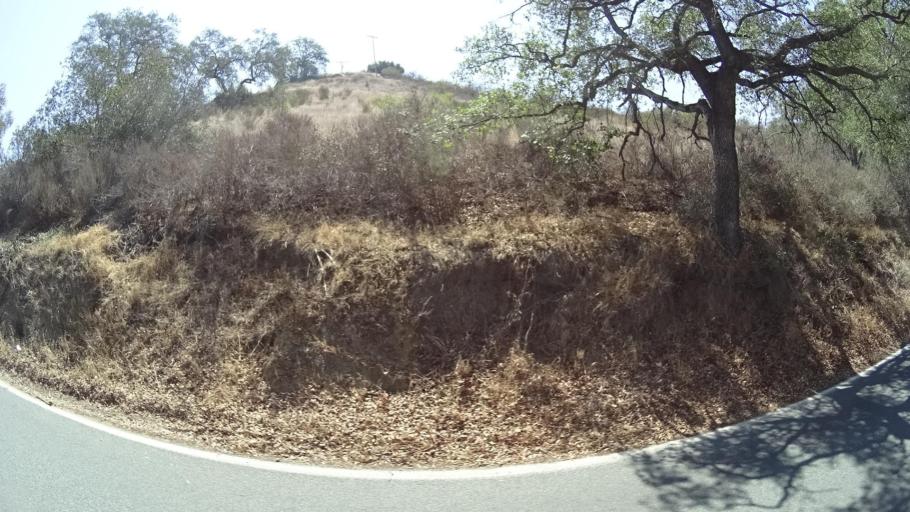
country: US
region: California
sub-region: San Diego County
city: Fallbrook
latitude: 33.4128
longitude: -117.2841
